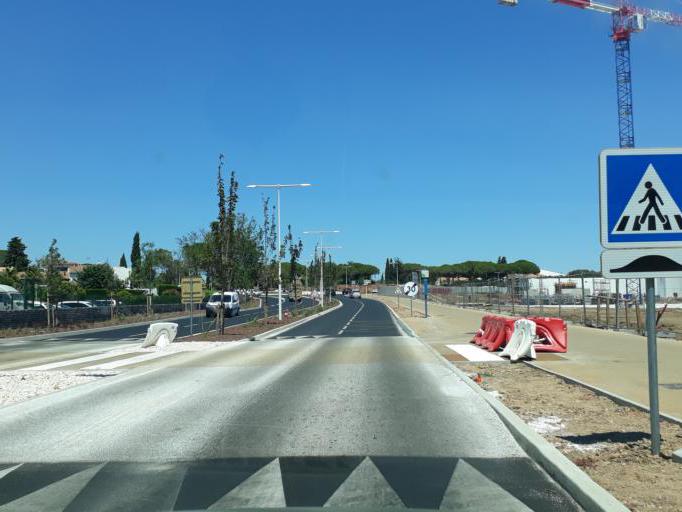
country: FR
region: Languedoc-Roussillon
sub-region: Departement de l'Herault
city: Le Cap d'Agde
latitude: 43.2873
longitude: 3.5067
